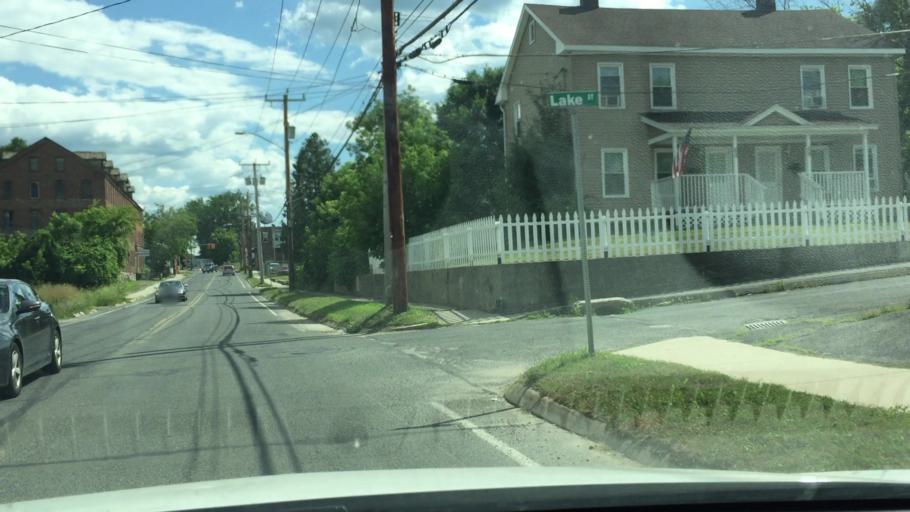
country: US
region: Massachusetts
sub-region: Berkshire County
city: Pittsfield
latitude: 42.4508
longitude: -73.2444
